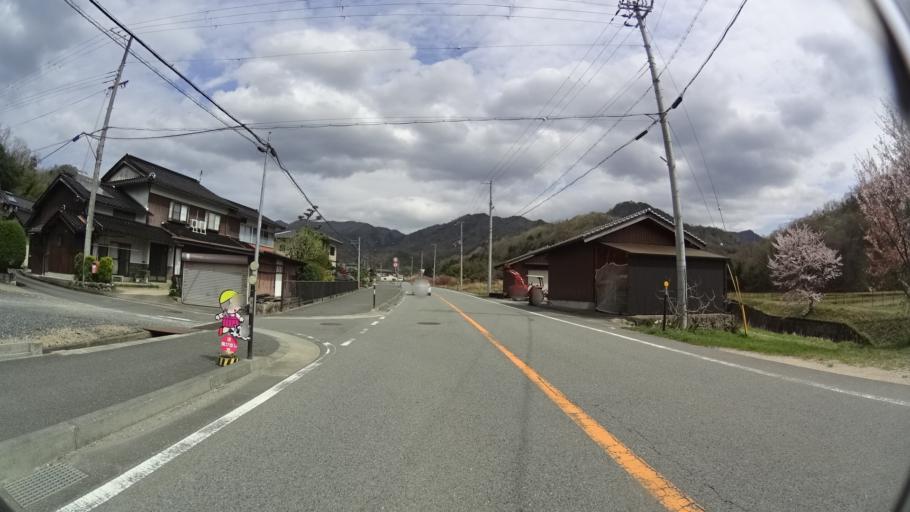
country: JP
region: Hyogo
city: Toyooka
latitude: 35.5021
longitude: 134.8795
